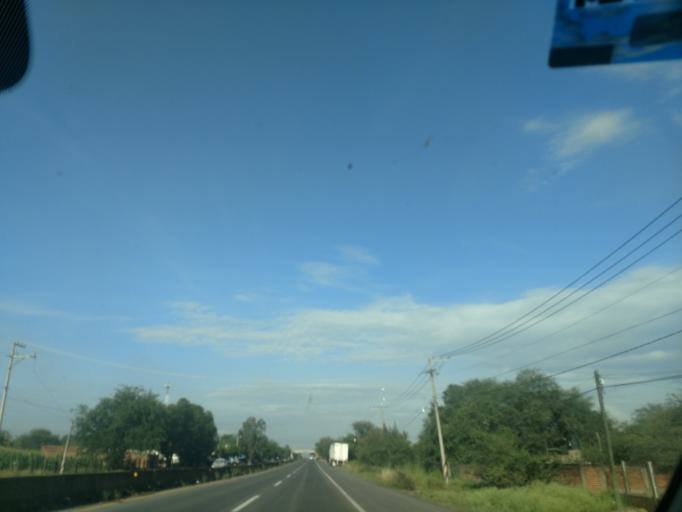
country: MX
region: Jalisco
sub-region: Ameca
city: Los Pocitos
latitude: 20.5374
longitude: -103.9327
